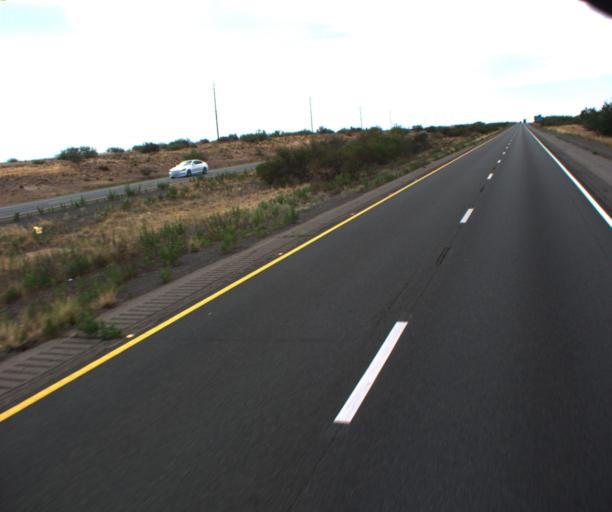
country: US
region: Arizona
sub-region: Yavapai County
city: Spring Valley
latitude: 34.3537
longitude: -112.1175
